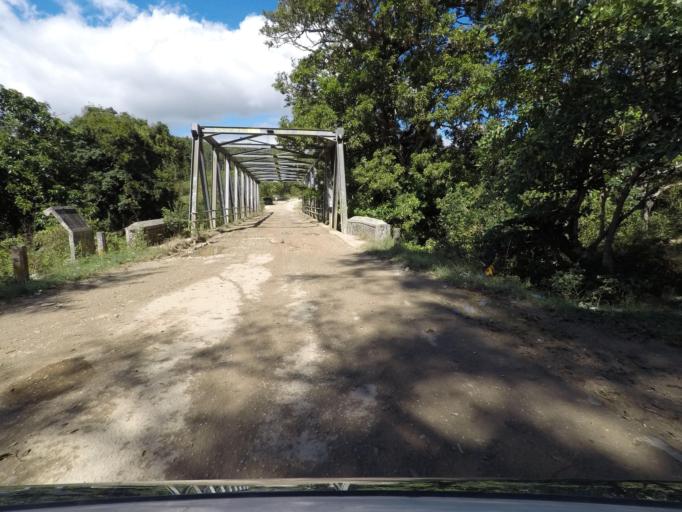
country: TL
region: Baucau
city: Venilale
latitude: -8.6665
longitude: 126.3697
